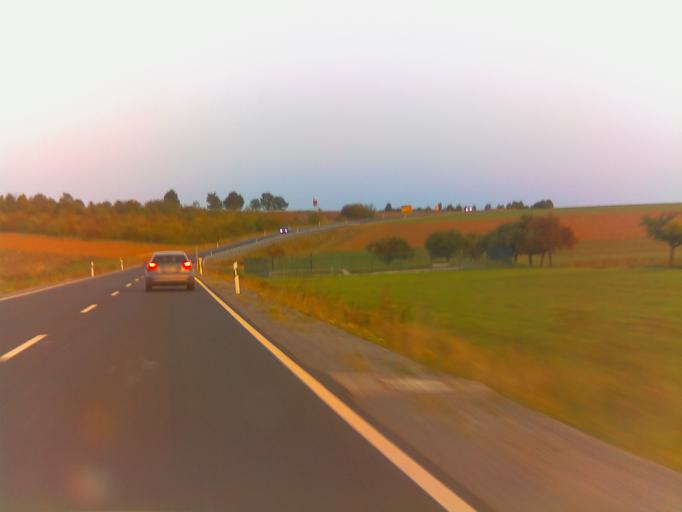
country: DE
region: Bavaria
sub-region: Regierungsbezirk Unterfranken
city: Oerlenbach
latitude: 50.1406
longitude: 10.1453
